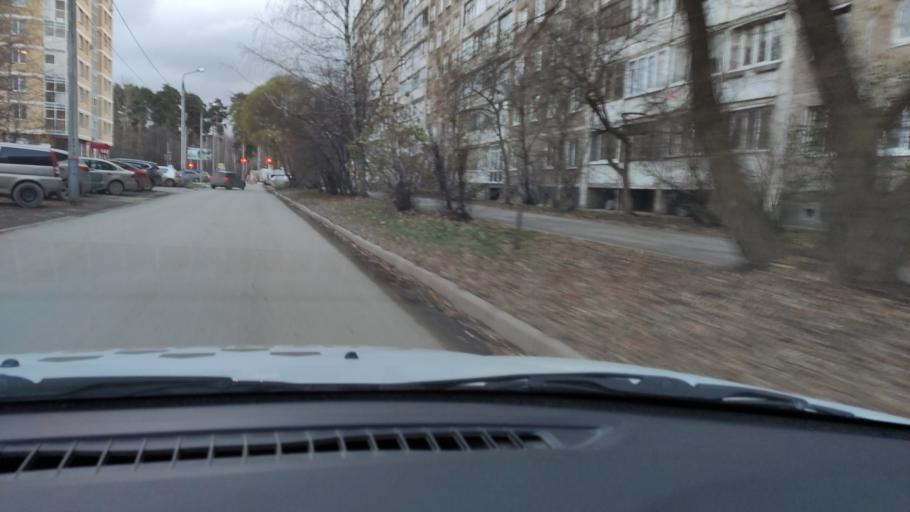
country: RU
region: Perm
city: Kondratovo
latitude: 57.9954
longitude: 56.1562
